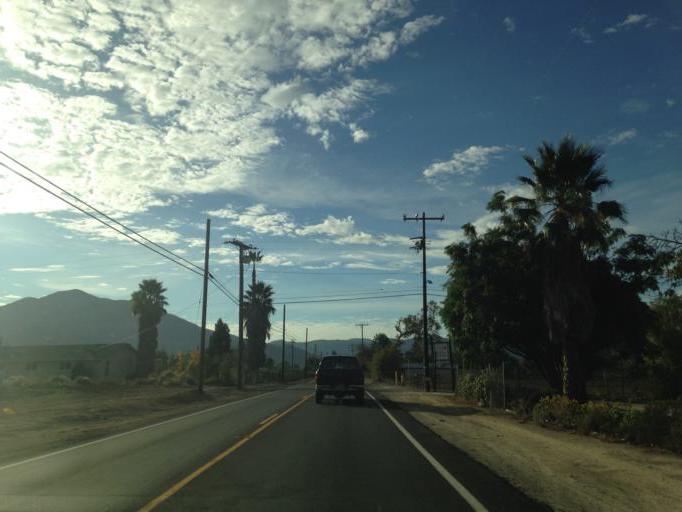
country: US
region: California
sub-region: San Diego County
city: Rainbow
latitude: 33.3716
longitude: -117.0783
